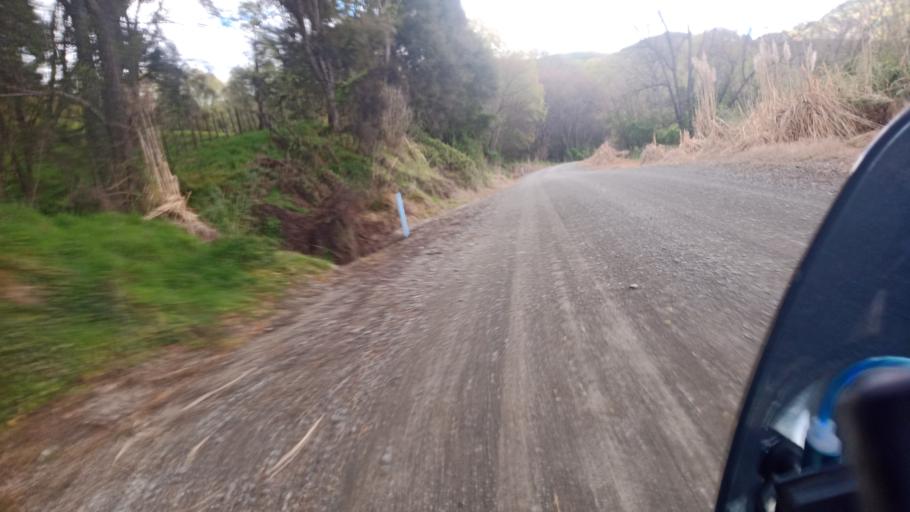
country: NZ
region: Gisborne
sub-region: Gisborne District
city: Gisborne
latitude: -38.2052
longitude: 178.2510
